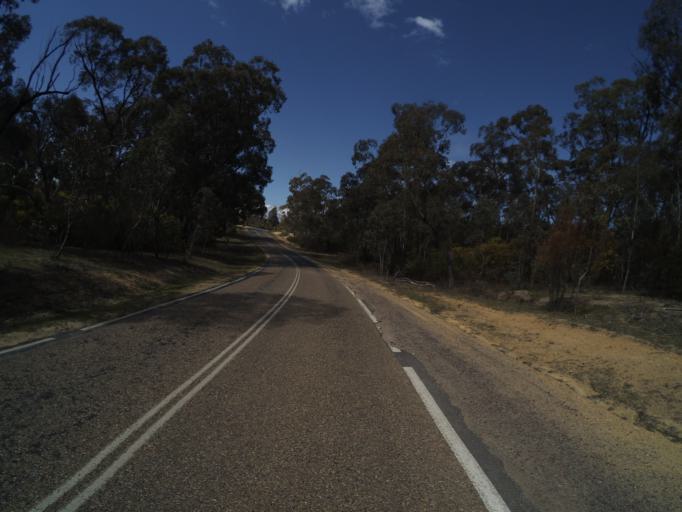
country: AU
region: Australian Capital Territory
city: Macquarie
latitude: -35.3508
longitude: 148.9371
